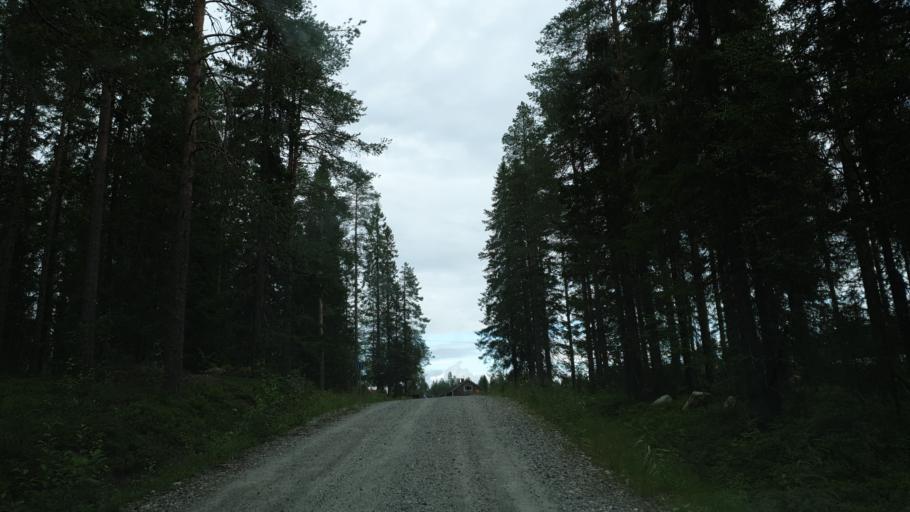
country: FI
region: Kainuu
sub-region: Kehys-Kainuu
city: Kuhmo
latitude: 64.4604
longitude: 29.5832
